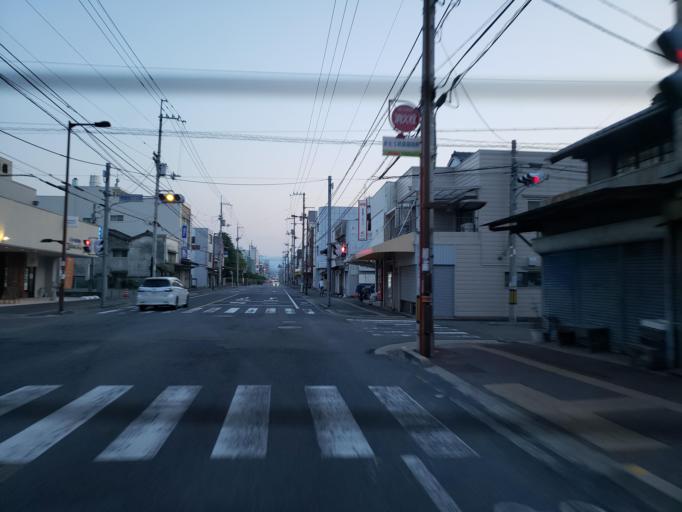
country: JP
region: Ehime
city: Hojo
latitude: 34.0574
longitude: 132.9902
